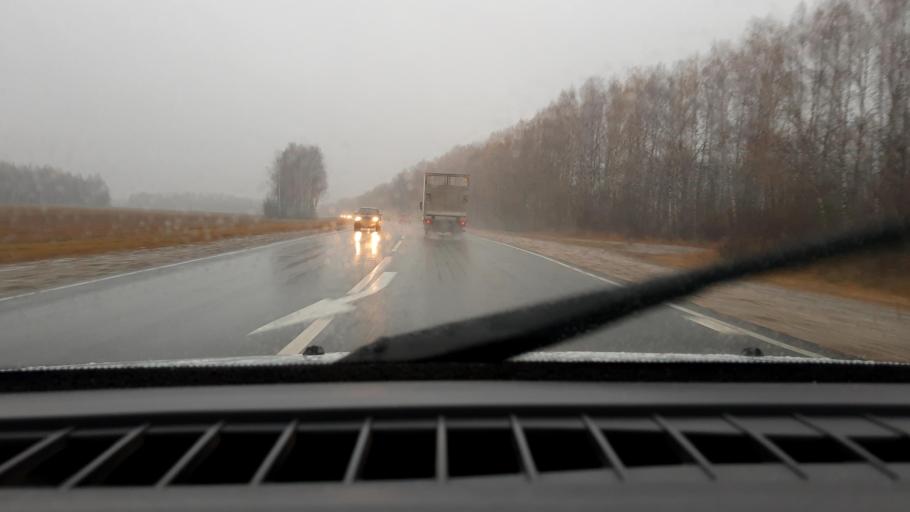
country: RU
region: Nizjnij Novgorod
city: Linda
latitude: 56.5778
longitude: 44.0226
